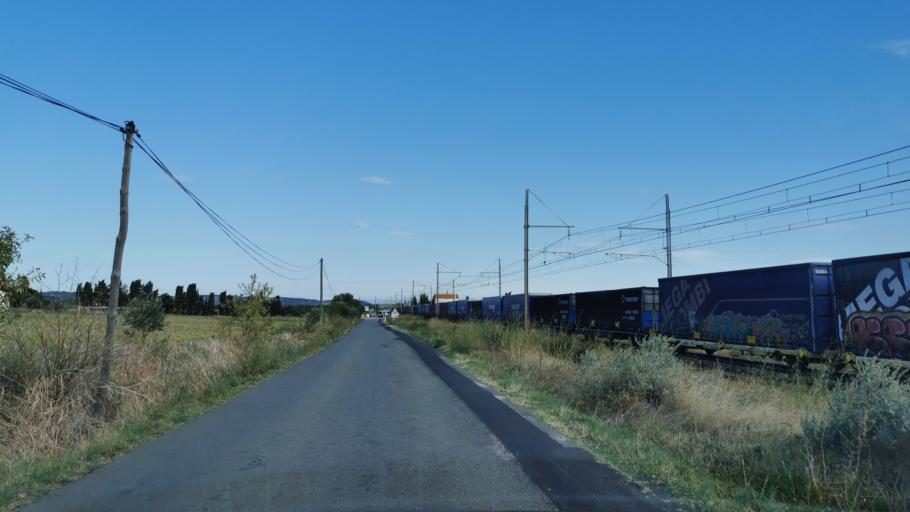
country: FR
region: Languedoc-Roussillon
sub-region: Departement de l'Aude
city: Narbonne
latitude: 43.1565
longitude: 3.0131
